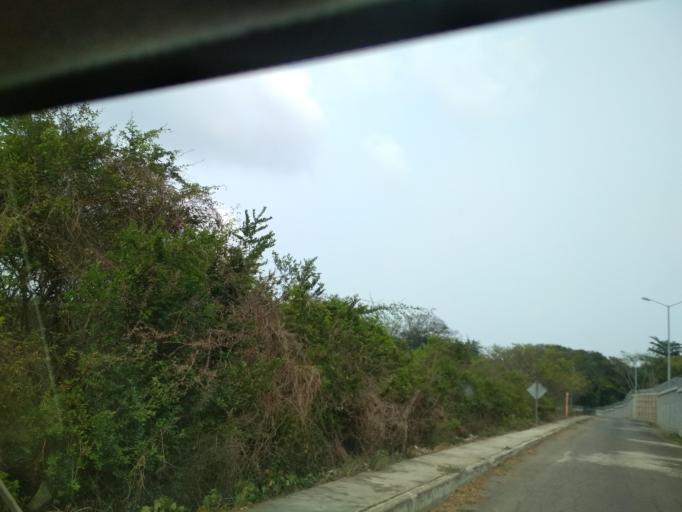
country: MX
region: Veracruz
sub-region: Medellin
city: Fraccionamiento Arboledas San Ramon
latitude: 19.0901
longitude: -96.1462
